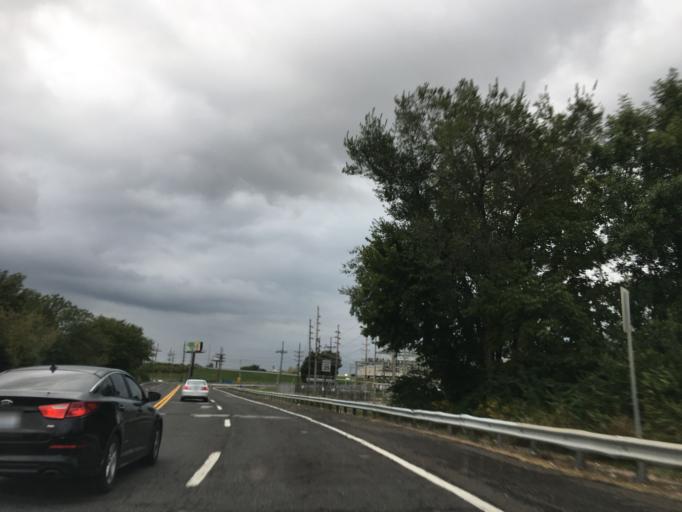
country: US
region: Missouri
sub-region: Saint Louis County
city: Berkeley
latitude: 38.7574
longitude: -90.3351
